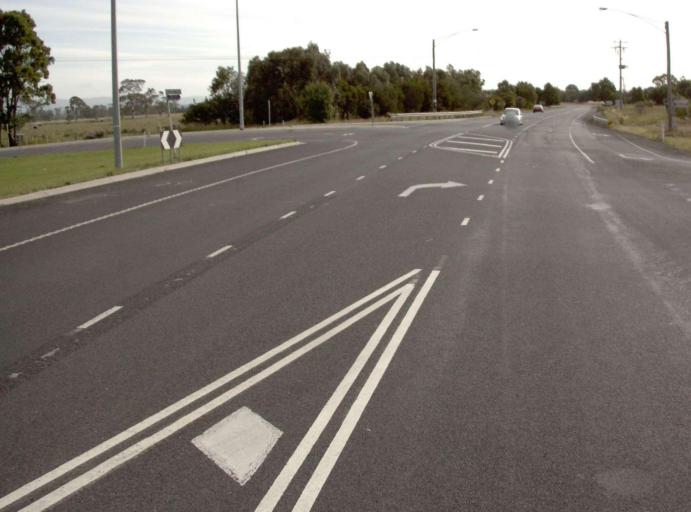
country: AU
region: Victoria
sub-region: Latrobe
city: Traralgon
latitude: -38.1285
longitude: 146.5642
